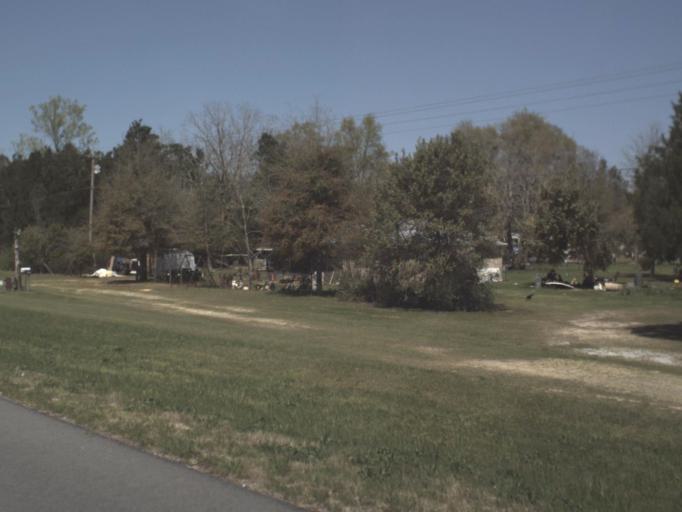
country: US
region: Florida
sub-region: Walton County
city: DeFuniak Springs
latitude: 30.7414
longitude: -86.1894
